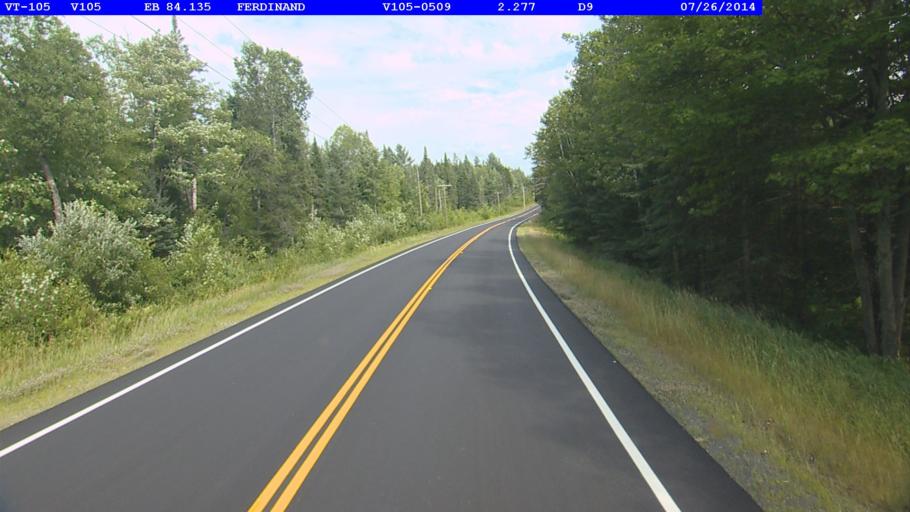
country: US
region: New Hampshire
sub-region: Coos County
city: Stratford
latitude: 44.7798
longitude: -71.7593
